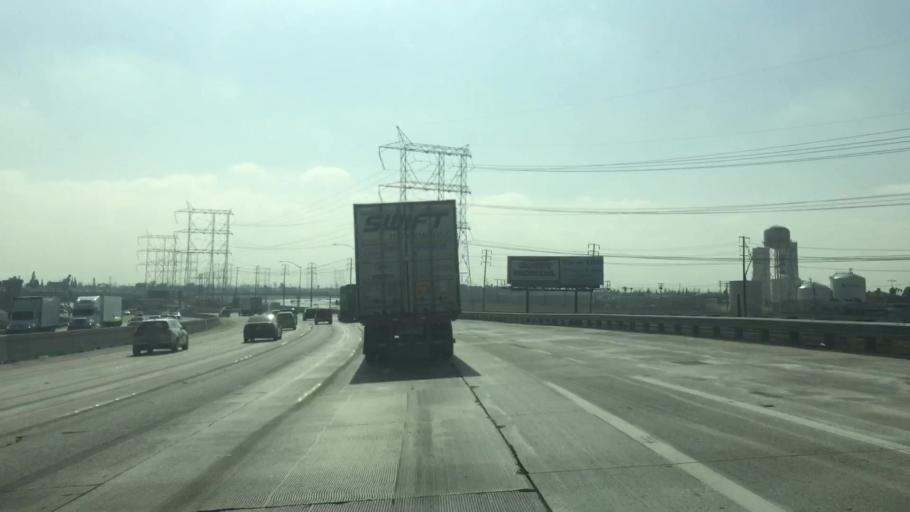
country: US
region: California
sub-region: Los Angeles County
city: Maywood
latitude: 33.9939
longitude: -118.1765
